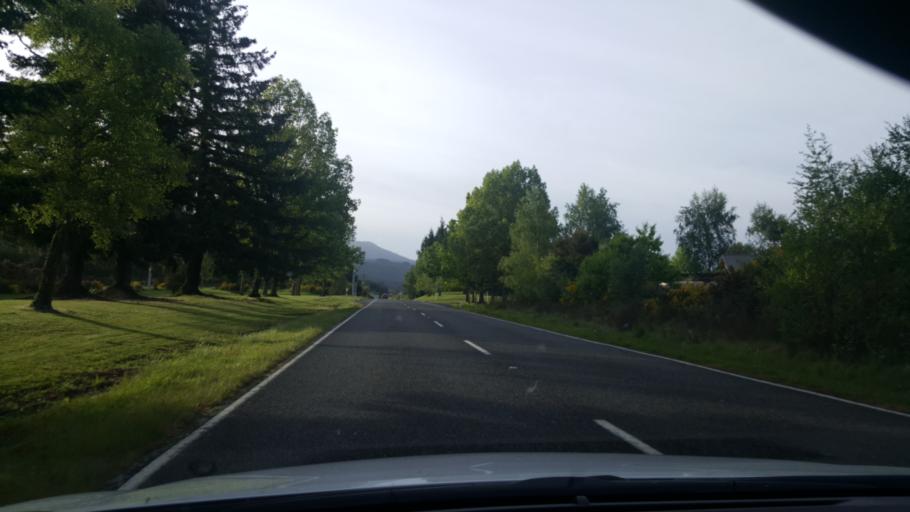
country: NZ
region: Waikato
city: Turangi
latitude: -38.9915
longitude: 175.7952
